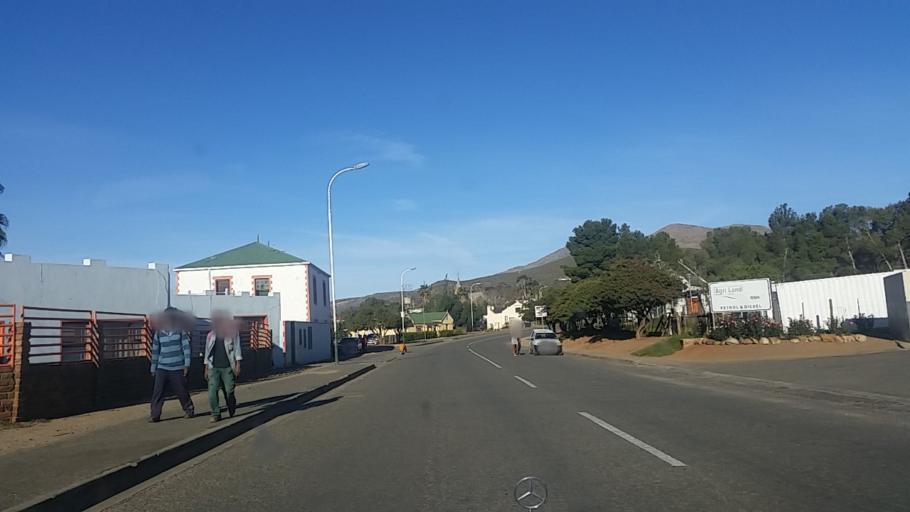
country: ZA
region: Western Cape
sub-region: Eden District Municipality
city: Knysna
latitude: -33.6587
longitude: 23.1190
